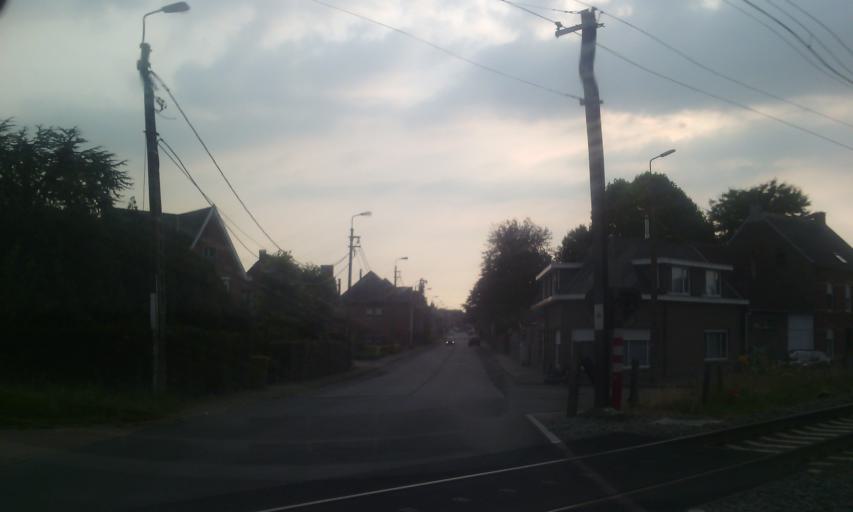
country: BE
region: Flanders
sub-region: Provincie Oost-Vlaanderen
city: Lede
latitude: 50.9647
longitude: 3.9969
